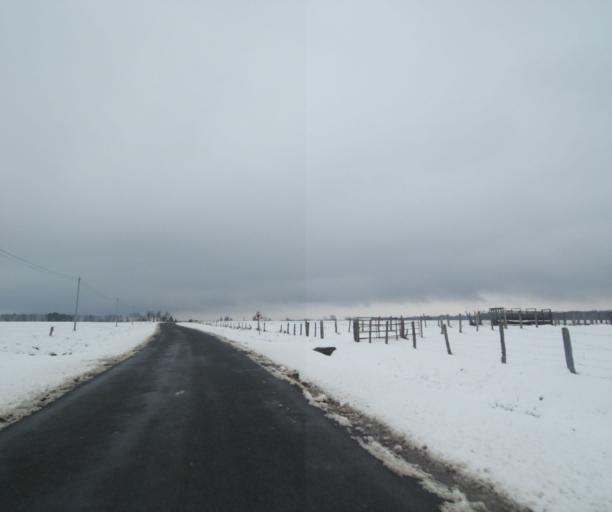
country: FR
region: Champagne-Ardenne
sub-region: Departement de la Haute-Marne
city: Laneuville-a-Remy
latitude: 48.5001
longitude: 4.8687
